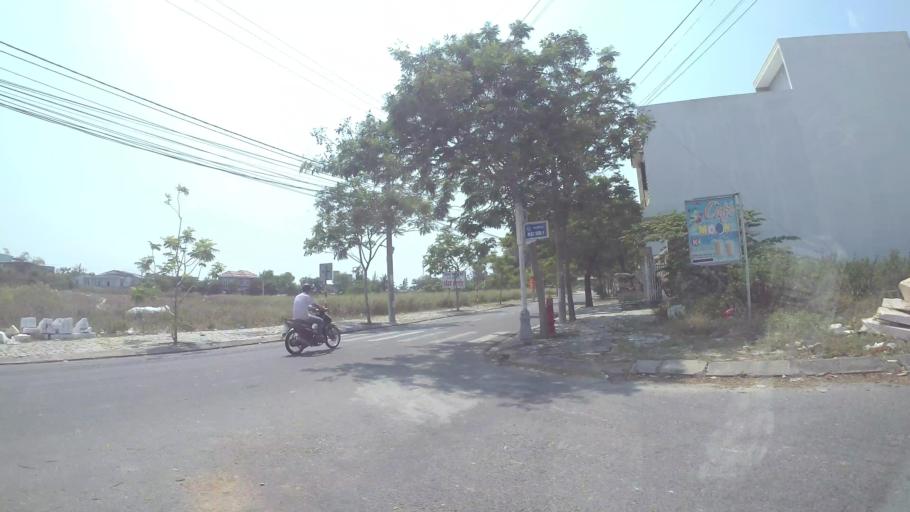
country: VN
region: Da Nang
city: Ngu Hanh Son
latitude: 16.0005
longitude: 108.2650
